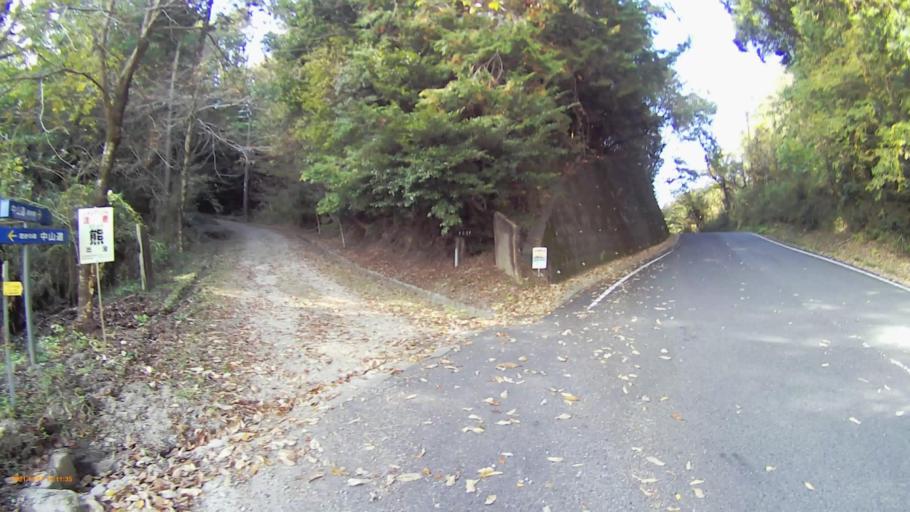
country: JP
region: Gifu
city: Mizunami
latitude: 35.4280
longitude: 137.2190
